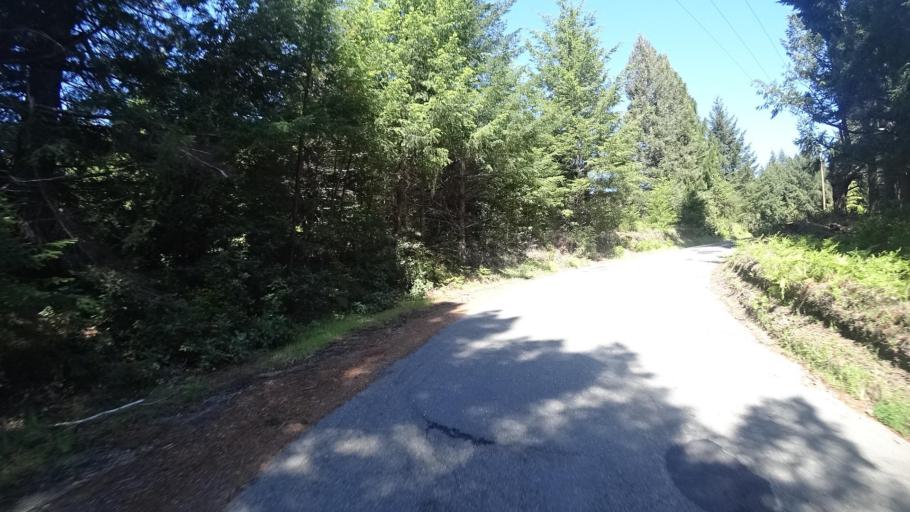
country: US
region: California
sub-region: Humboldt County
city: Redway
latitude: 40.1839
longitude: -124.0898
